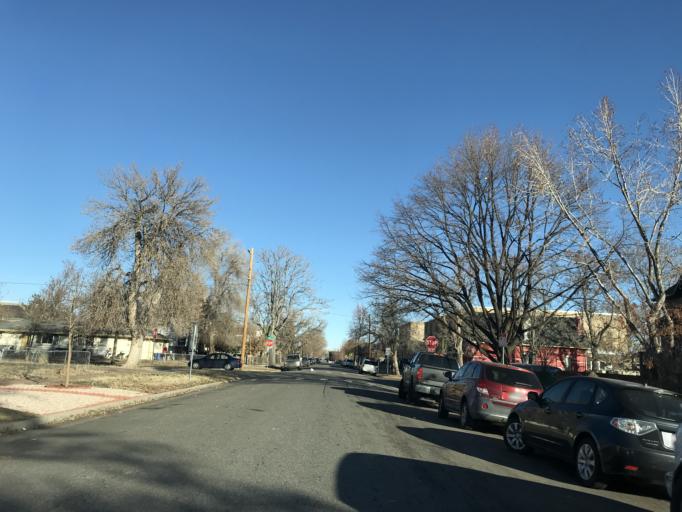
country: US
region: Colorado
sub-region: Denver County
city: Denver
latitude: 39.7652
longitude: -104.9709
